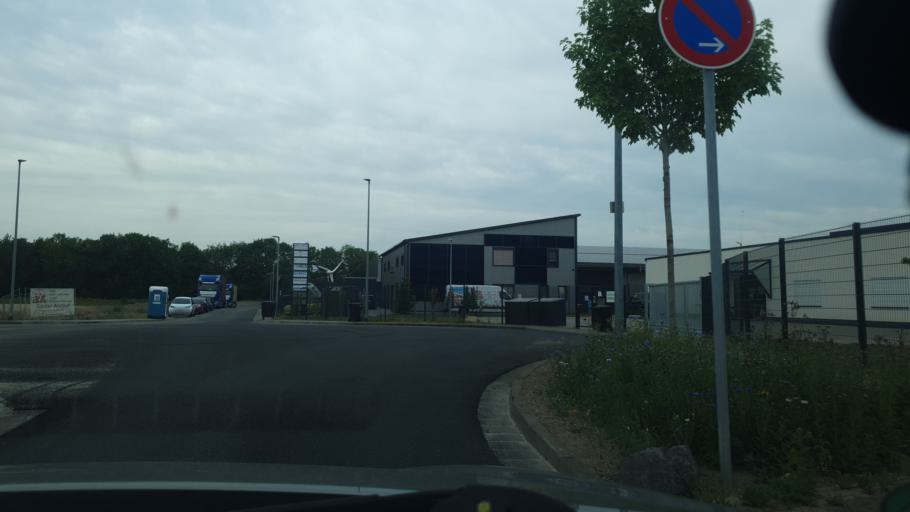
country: DE
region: Rheinland-Pfalz
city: Andernach
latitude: 50.4179
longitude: 7.4174
